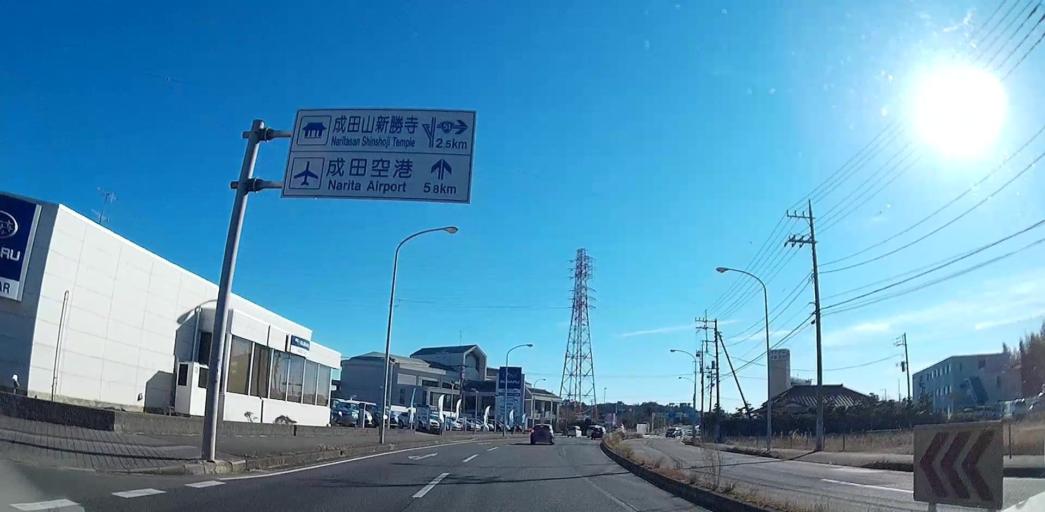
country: JP
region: Chiba
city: Narita
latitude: 35.7913
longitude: 140.3270
